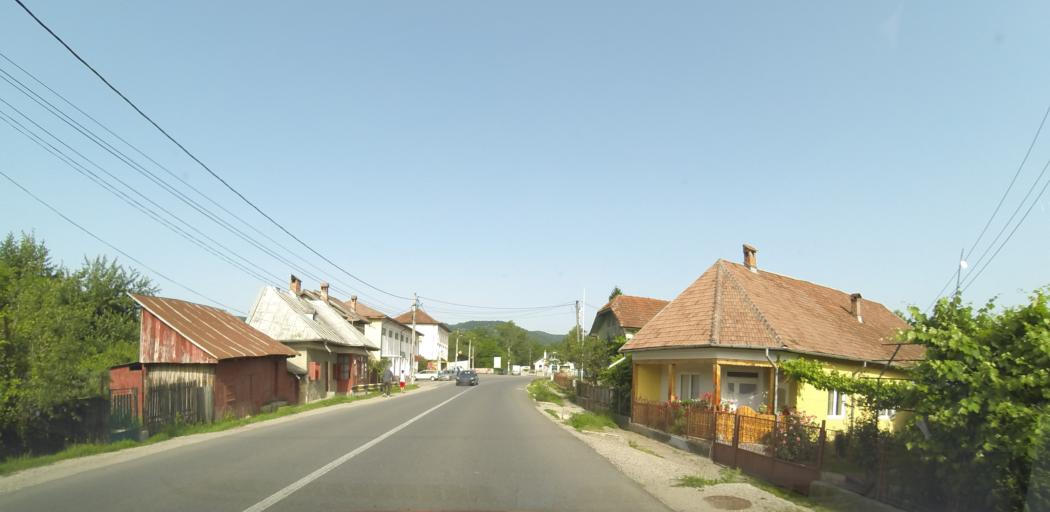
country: RO
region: Valcea
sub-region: Comuna Pausesti-Maglasi
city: Pausesti-Maglasi
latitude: 45.1356
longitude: 24.2501
